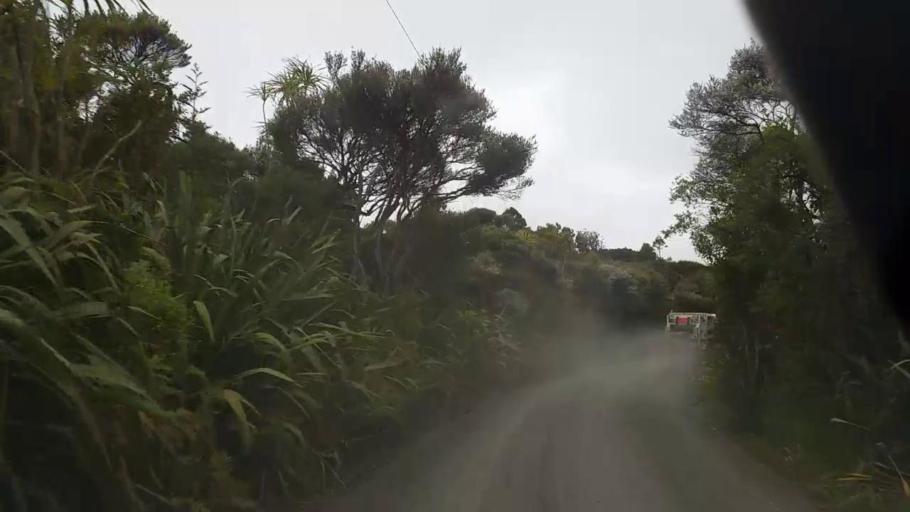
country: NZ
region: Auckland
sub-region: Auckland
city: Muriwai Beach
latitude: -36.9256
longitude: 174.4901
